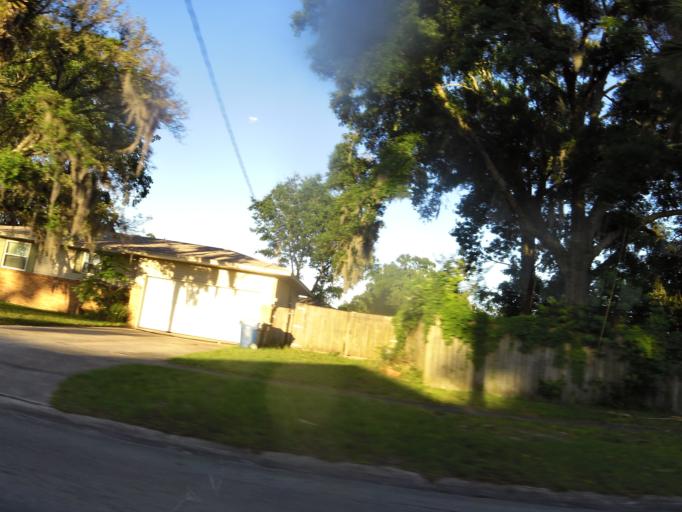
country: US
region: Florida
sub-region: Duval County
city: Jacksonville
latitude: 30.3383
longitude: -81.5685
